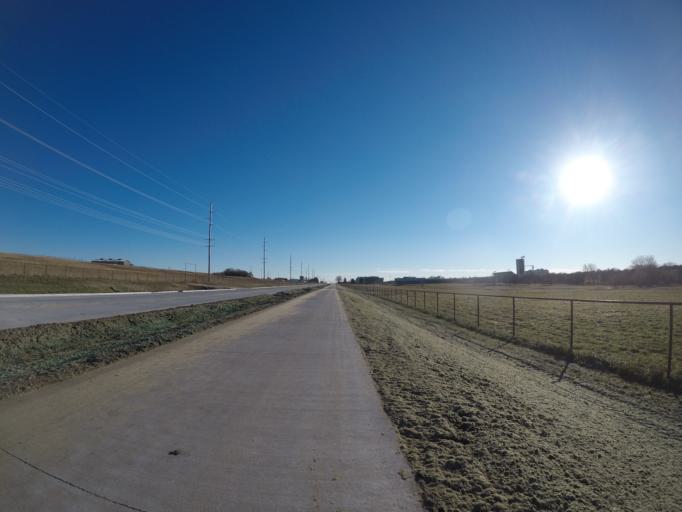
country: US
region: Kansas
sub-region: Riley County
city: Manhattan
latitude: 39.2113
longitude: -96.5858
